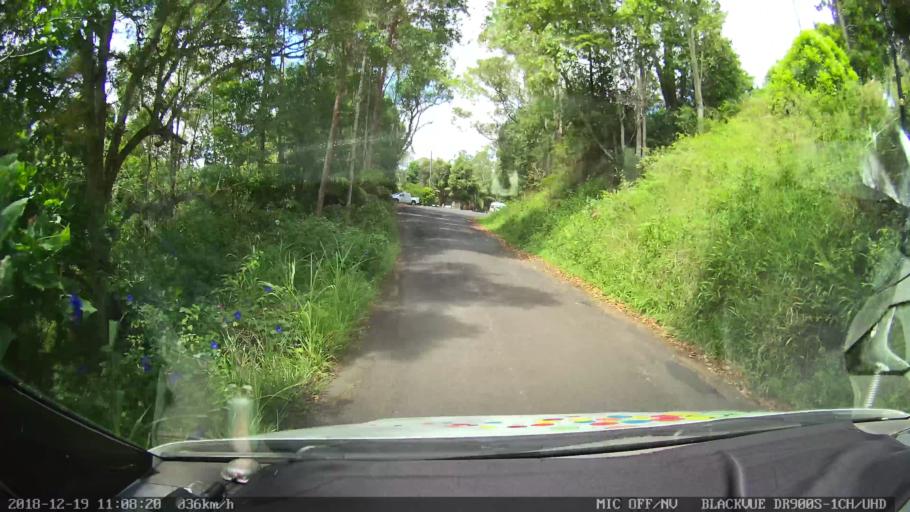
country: AU
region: New South Wales
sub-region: Lismore Municipality
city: Nimbin
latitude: -28.6305
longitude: 153.2662
